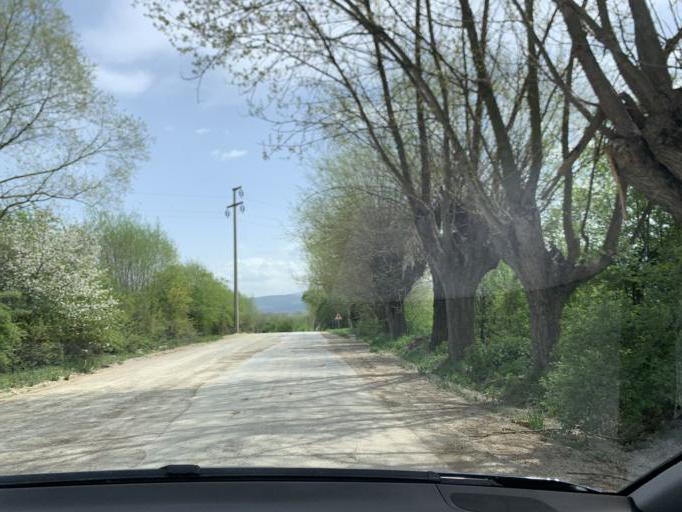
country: TR
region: Bolu
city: Bolu
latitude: 40.7605
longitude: 31.6978
